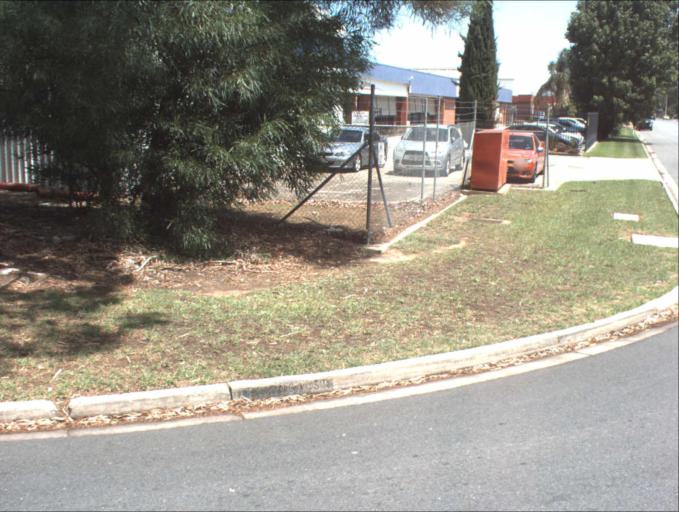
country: AU
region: South Australia
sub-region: Port Adelaide Enfield
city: Blair Athol
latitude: -34.8601
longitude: 138.5740
